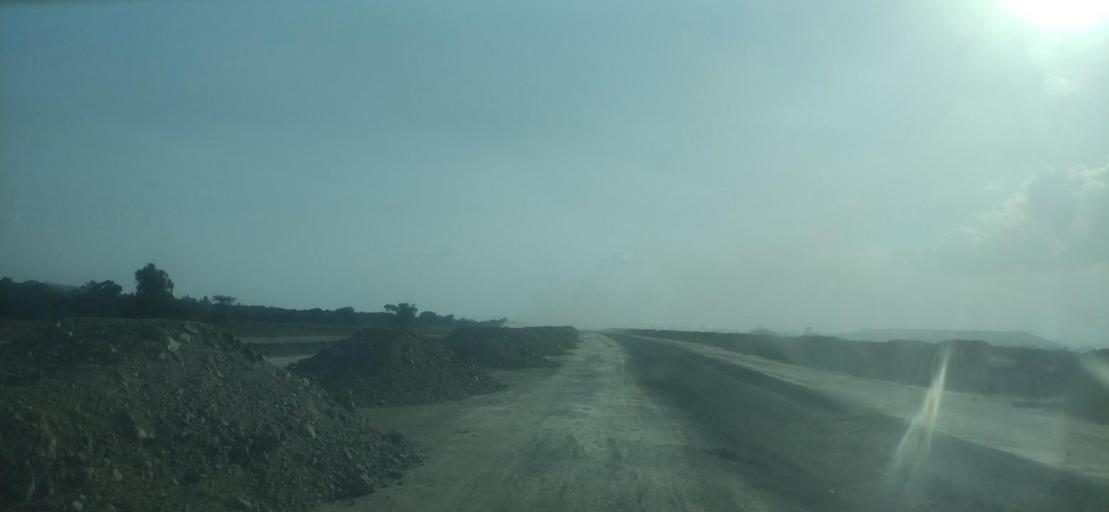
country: ET
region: Southern Nations, Nationalities, and People's Region
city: Hawassa
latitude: 7.1713
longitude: 38.4894
